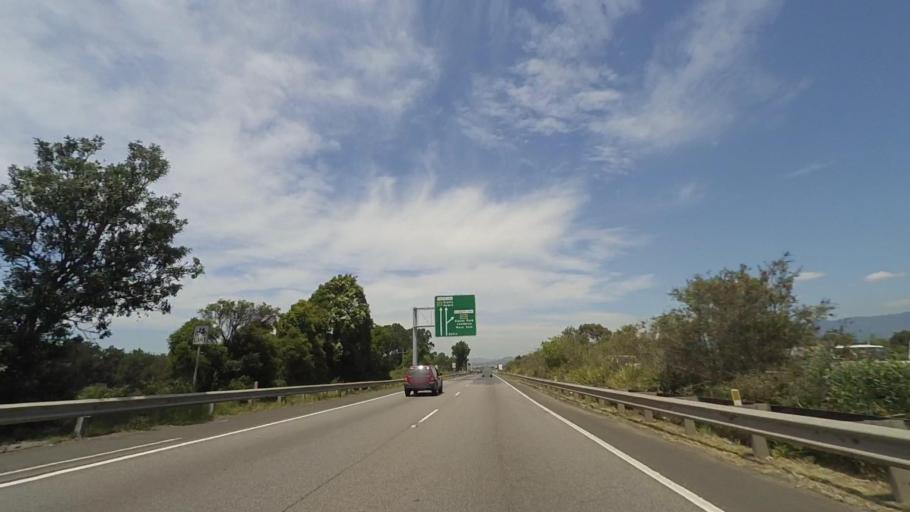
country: AU
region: New South Wales
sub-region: Shellharbour
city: Albion Park Rail
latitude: -34.5450
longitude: 150.7852
